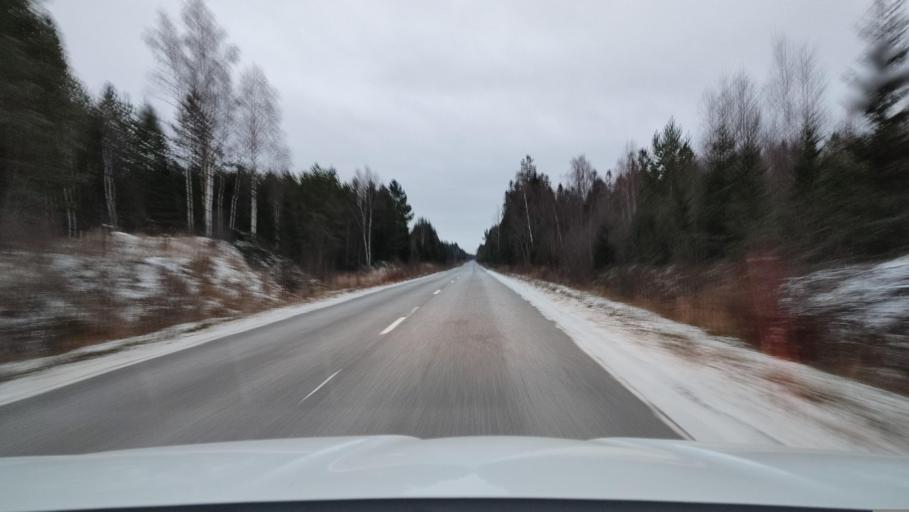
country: FI
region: Ostrobothnia
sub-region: Vaasa
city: Replot
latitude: 63.2573
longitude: 21.3663
